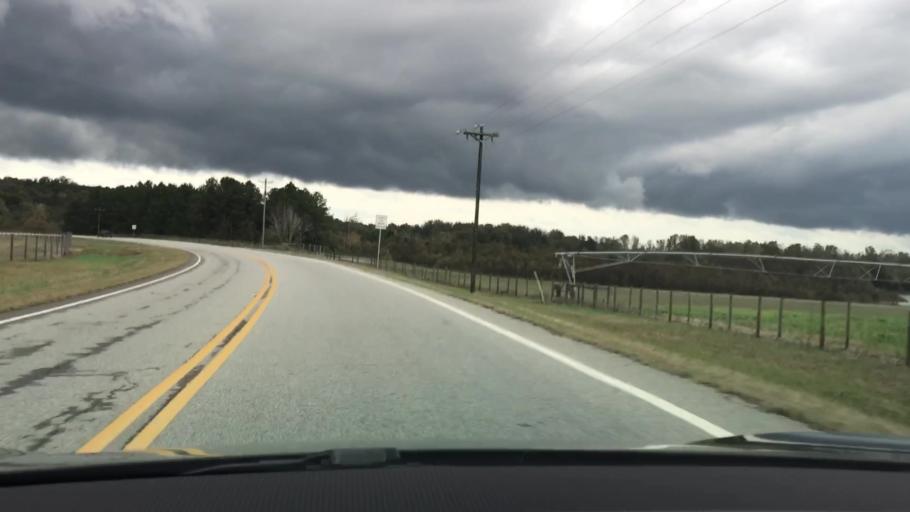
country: US
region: Georgia
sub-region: Oconee County
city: Watkinsville
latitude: 33.7243
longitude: -83.3017
